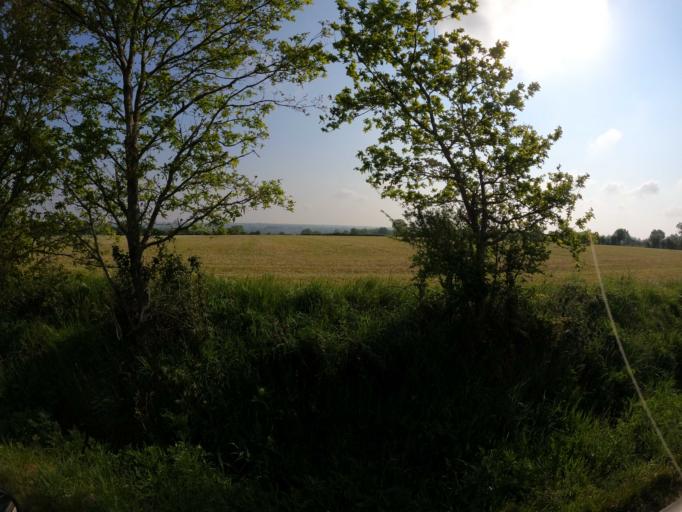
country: FR
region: Pays de la Loire
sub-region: Departement de Maine-et-Loire
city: La Romagne
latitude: 47.0658
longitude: -1.0440
